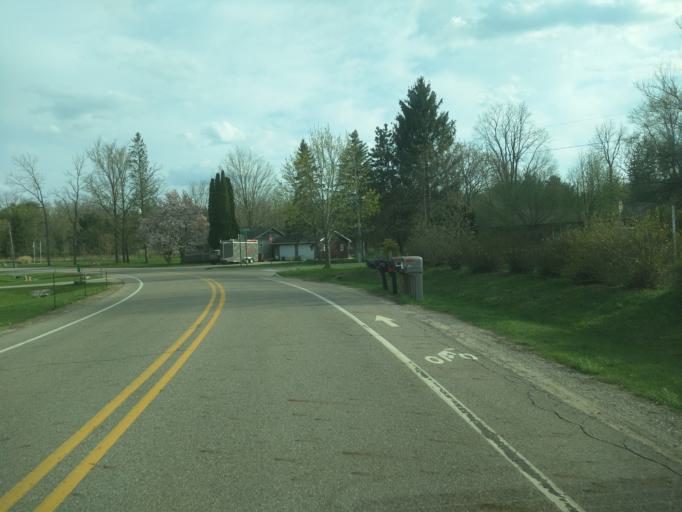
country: US
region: Michigan
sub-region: Eaton County
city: Dimondale
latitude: 42.6411
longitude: -84.6493
